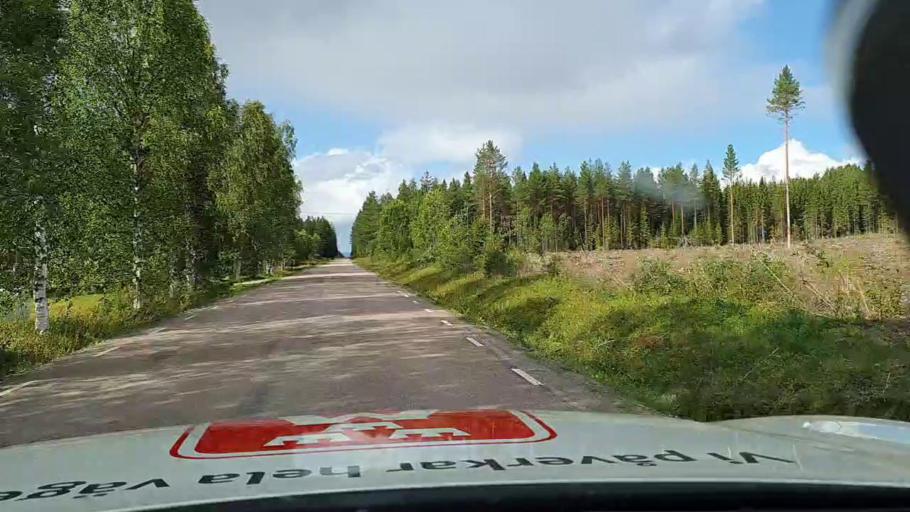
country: SE
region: Jaemtland
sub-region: Stroemsunds Kommun
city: Stroemsund
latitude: 63.8658
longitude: 15.3791
